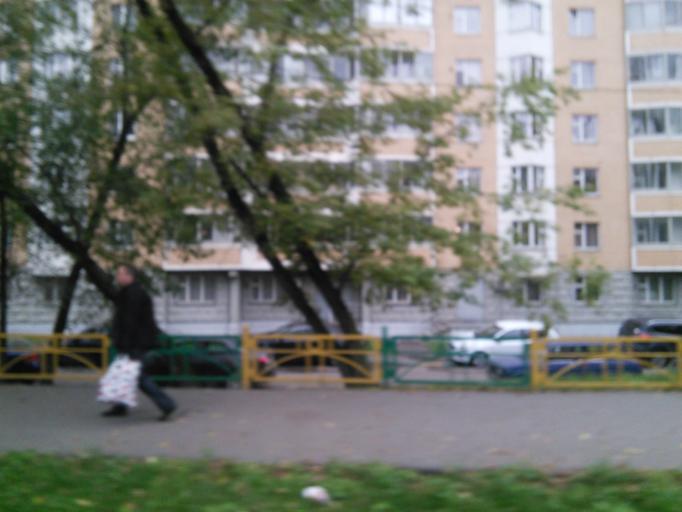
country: RU
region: Moskovskaya
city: Levoberezhnyy
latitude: 55.8651
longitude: 37.4775
